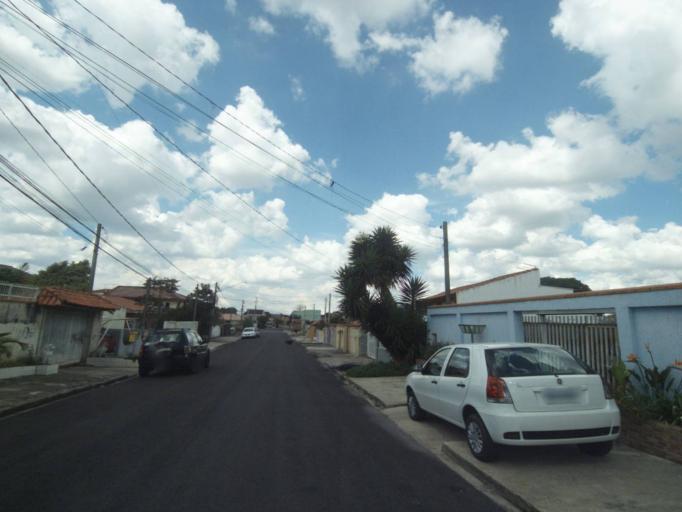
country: BR
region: Parana
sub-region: Pinhais
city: Pinhais
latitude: -25.4644
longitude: -49.2064
